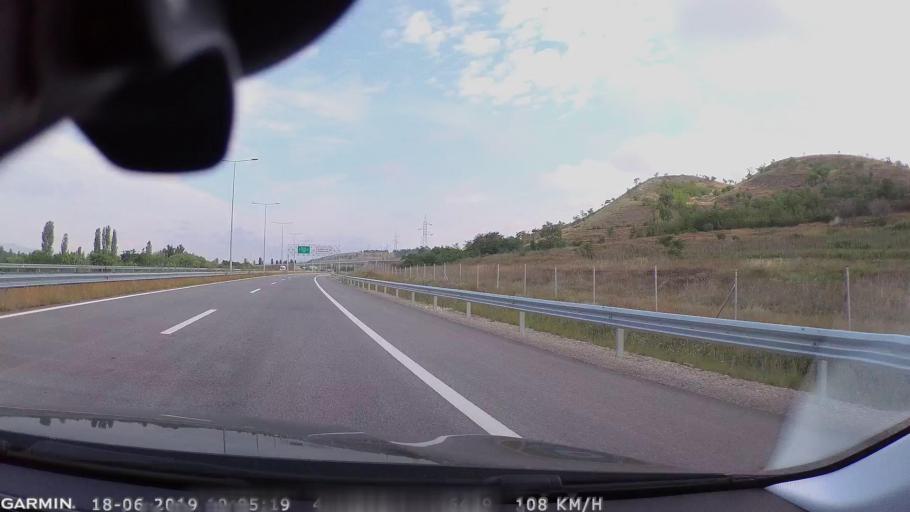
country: MK
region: Sveti Nikole
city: Sveti Nikole
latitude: 41.8530
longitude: 21.9644
